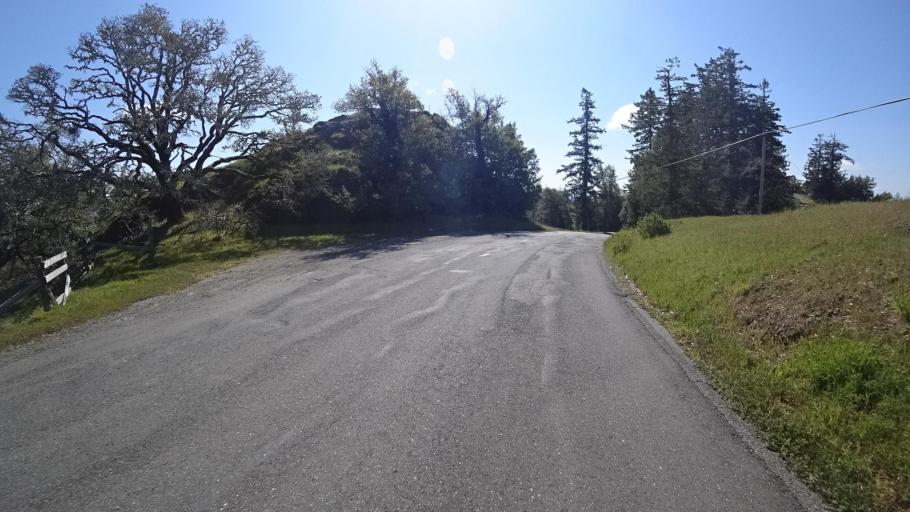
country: US
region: California
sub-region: Humboldt County
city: Redway
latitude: 40.0870
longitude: -123.6729
